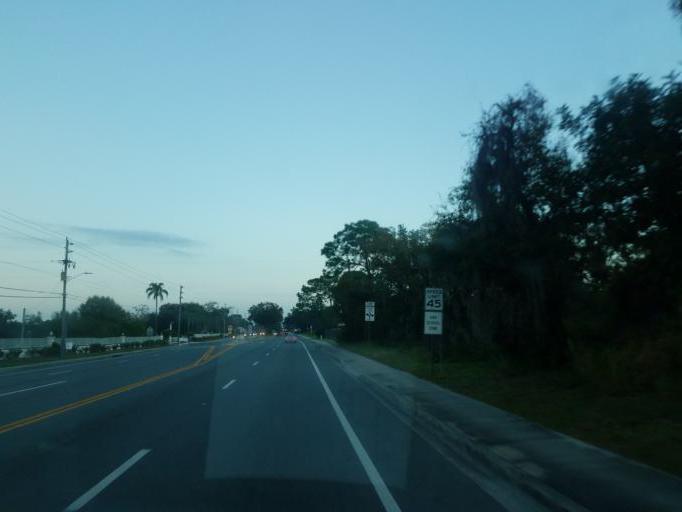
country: US
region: Florida
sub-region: Sarasota County
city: Kensington Park
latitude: 27.3635
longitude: -82.5056
